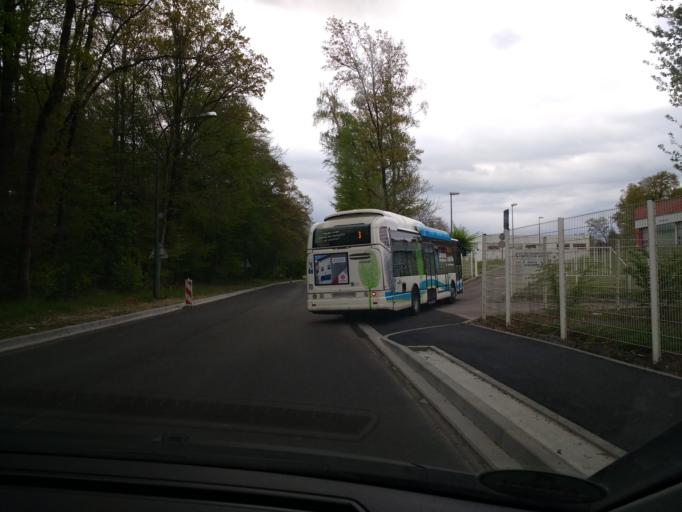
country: FR
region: Lorraine
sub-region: Departement de la Moselle
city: Remelfing
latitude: 49.1086
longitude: 7.0877
